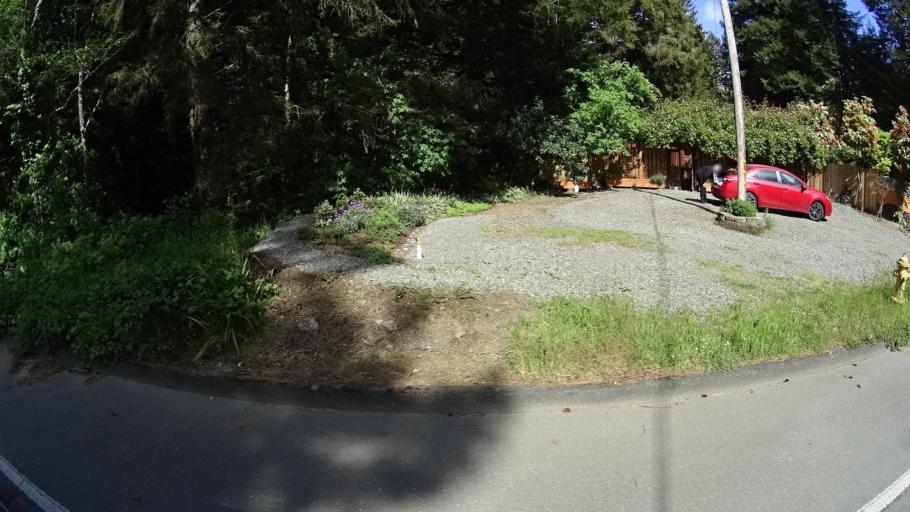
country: US
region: California
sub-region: Humboldt County
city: Pine Hills
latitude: 40.7503
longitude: -124.1460
